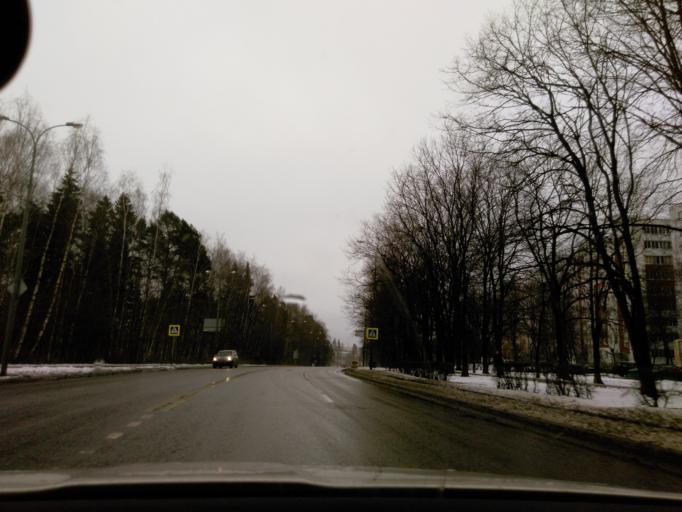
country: RU
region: Moskovskaya
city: Rzhavki
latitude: 55.9871
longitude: 37.2341
